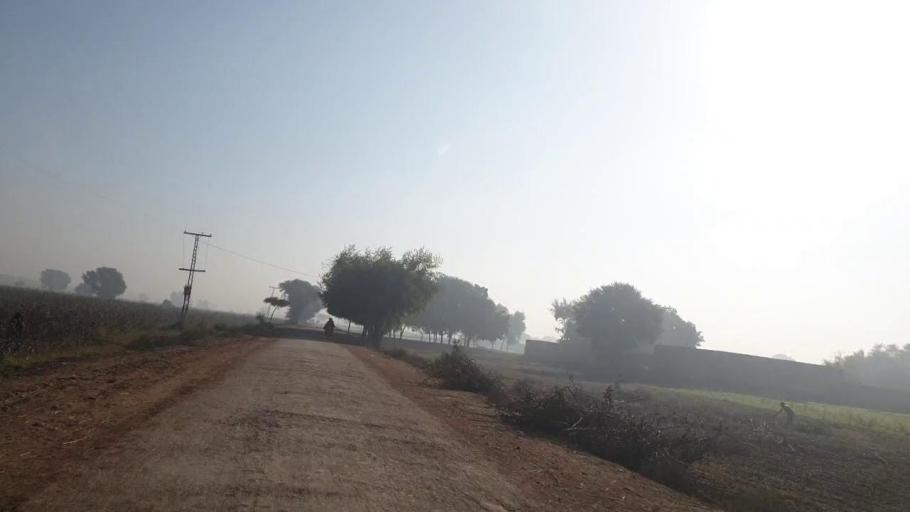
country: PK
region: Sindh
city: Dadu
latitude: 26.6753
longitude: 67.7907
